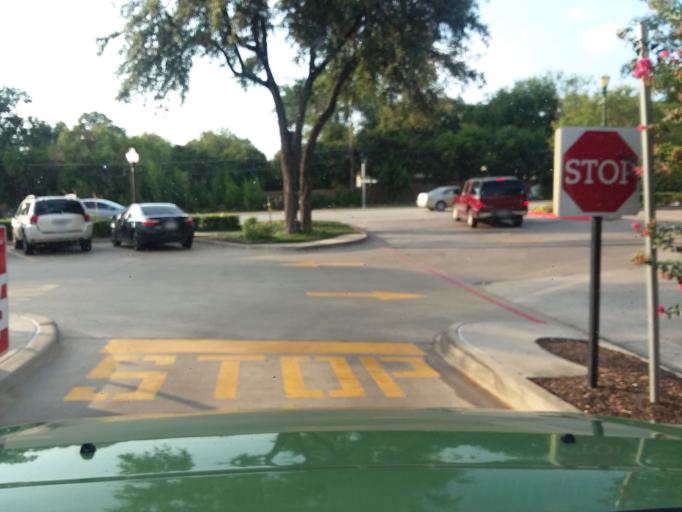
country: US
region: Texas
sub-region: Dallas County
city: University Park
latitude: 32.8615
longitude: -96.8520
